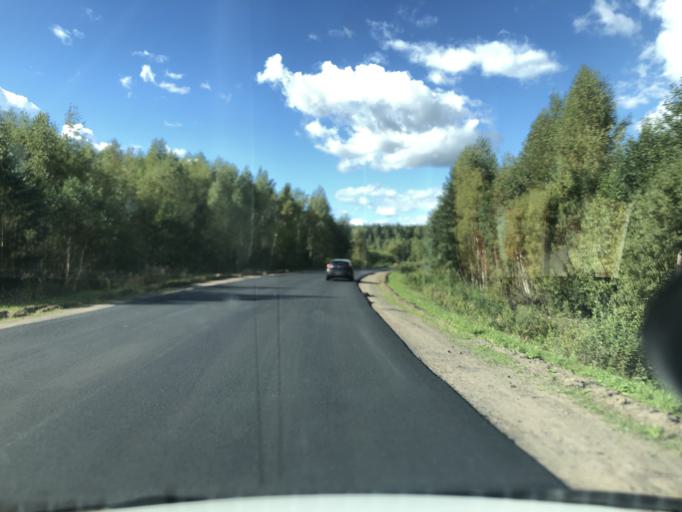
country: RU
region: Jaroslavl
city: Porech'ye-Rybnoye
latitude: 56.9720
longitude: 39.4127
